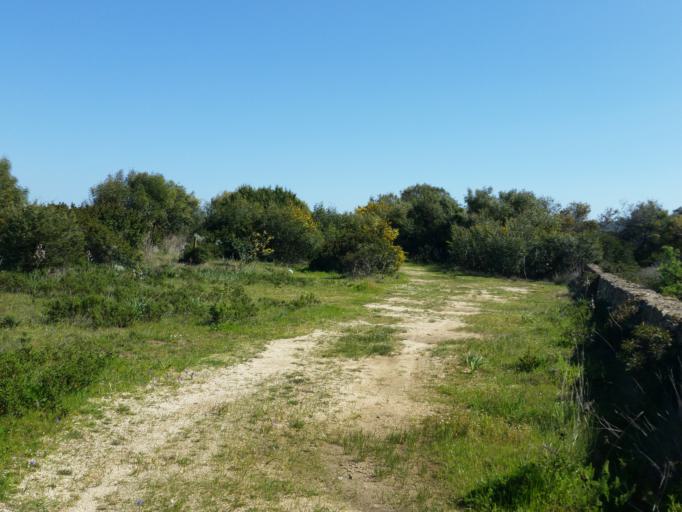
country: IT
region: Sardinia
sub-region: Provincia di Olbia-Tempio
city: Budoni
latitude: 40.7188
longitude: 9.7112
